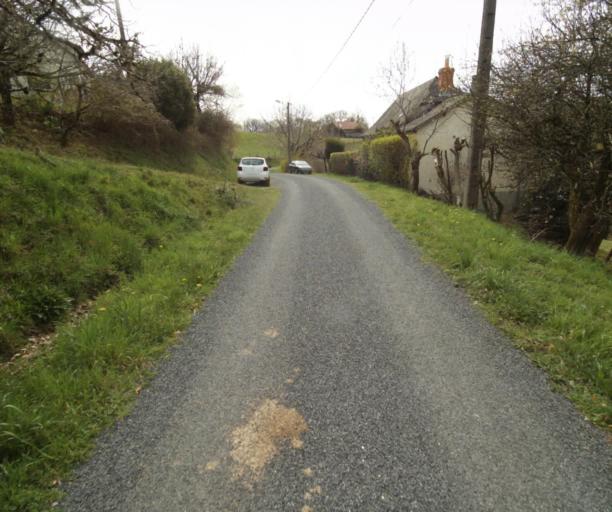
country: FR
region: Limousin
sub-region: Departement de la Correze
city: Sainte-Fortunade
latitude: 45.2034
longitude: 1.8539
